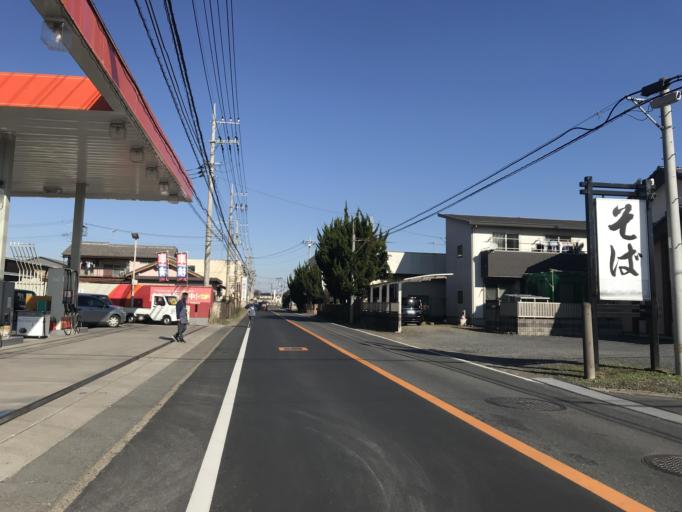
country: JP
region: Ibaraki
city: Yuki
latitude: 36.2780
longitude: 139.8530
